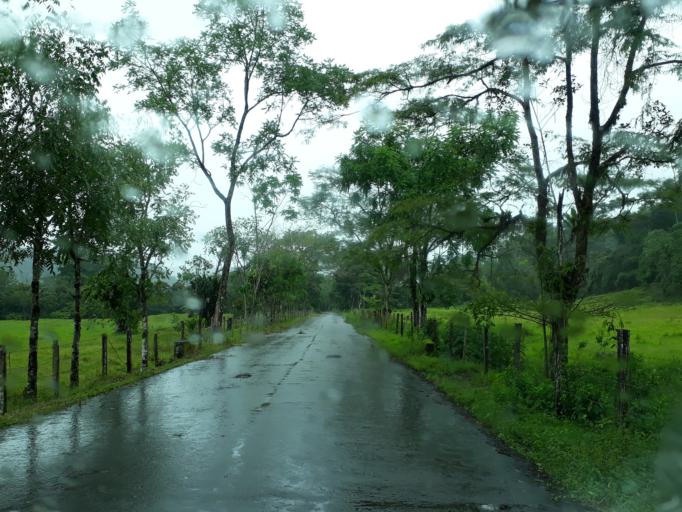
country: CO
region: Boyaca
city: Santa Maria
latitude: 4.7256
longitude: -73.2955
